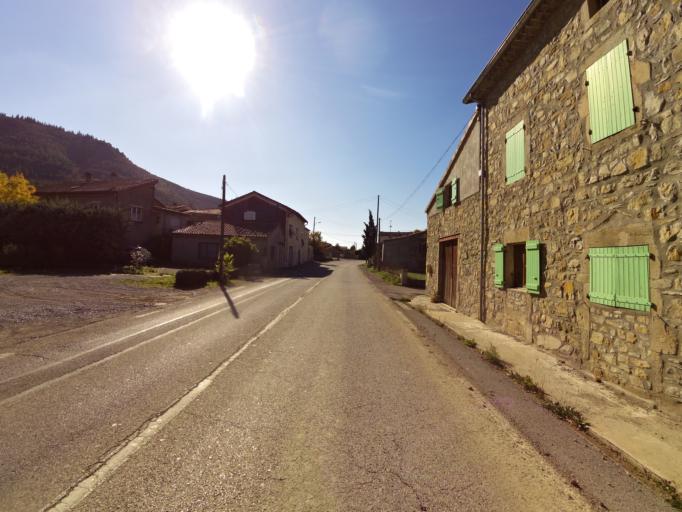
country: FR
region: Rhone-Alpes
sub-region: Departement de l'Ardeche
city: Vesseaux
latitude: 44.6472
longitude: 4.4384
